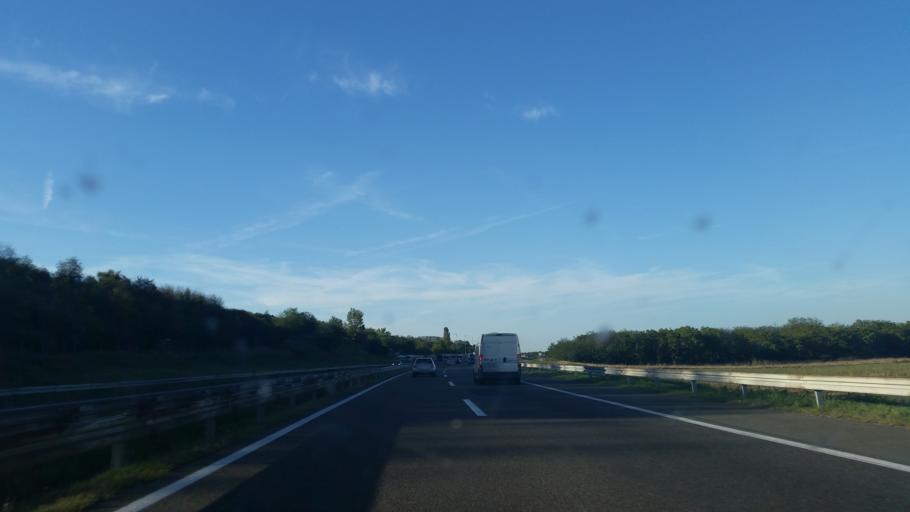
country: RS
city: Lugavcina
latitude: 44.4636
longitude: 21.0382
